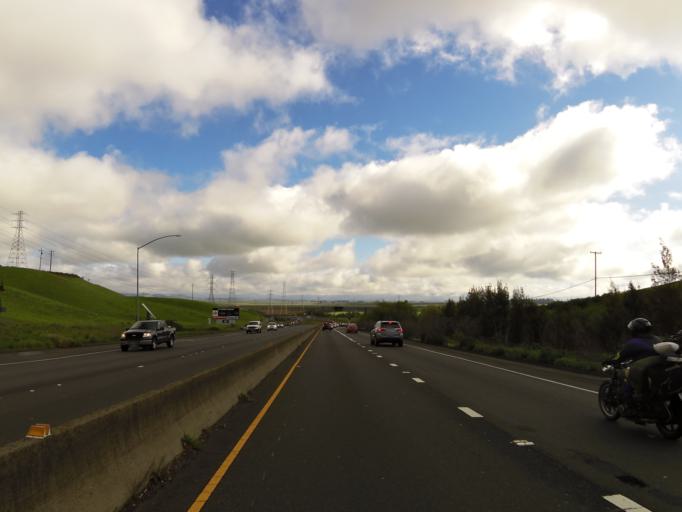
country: US
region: California
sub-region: Marin County
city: Black Point-Green Point
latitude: 38.1490
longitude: -122.4523
